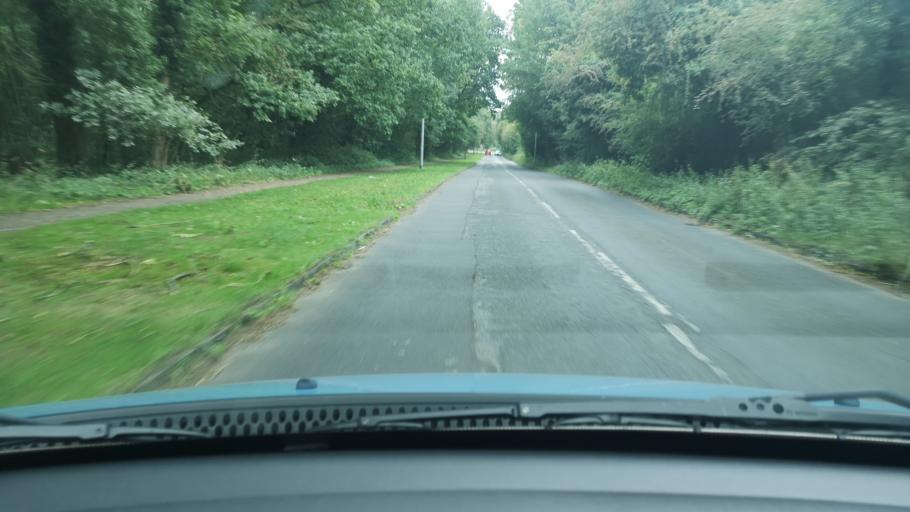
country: GB
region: England
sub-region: North Lincolnshire
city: Scunthorpe
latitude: 53.5843
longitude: -0.6798
